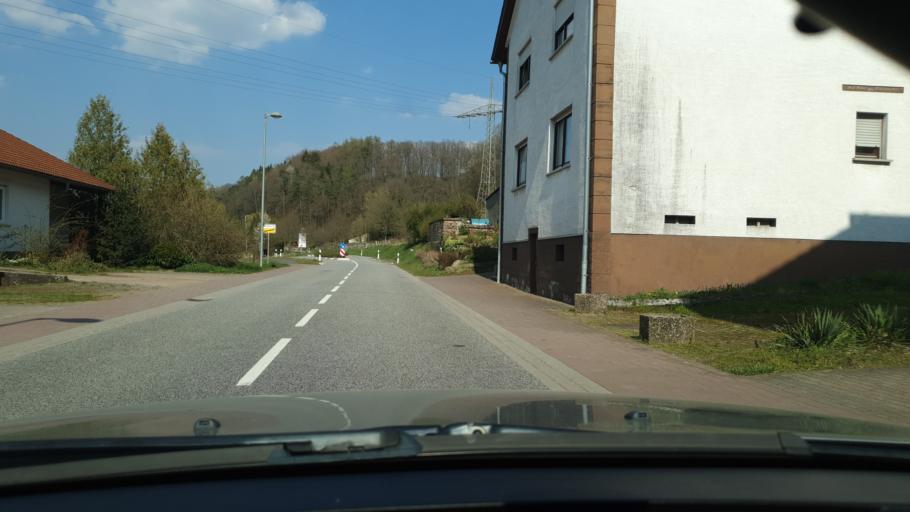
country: DE
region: Rheinland-Pfalz
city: Battweiler
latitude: 49.2967
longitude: 7.4650
